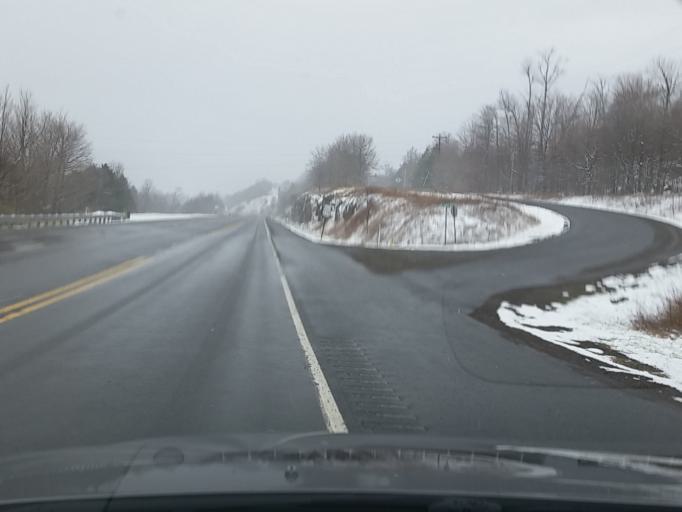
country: US
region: Pennsylvania
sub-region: Sullivan County
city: Laporte
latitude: 41.3868
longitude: -76.5085
